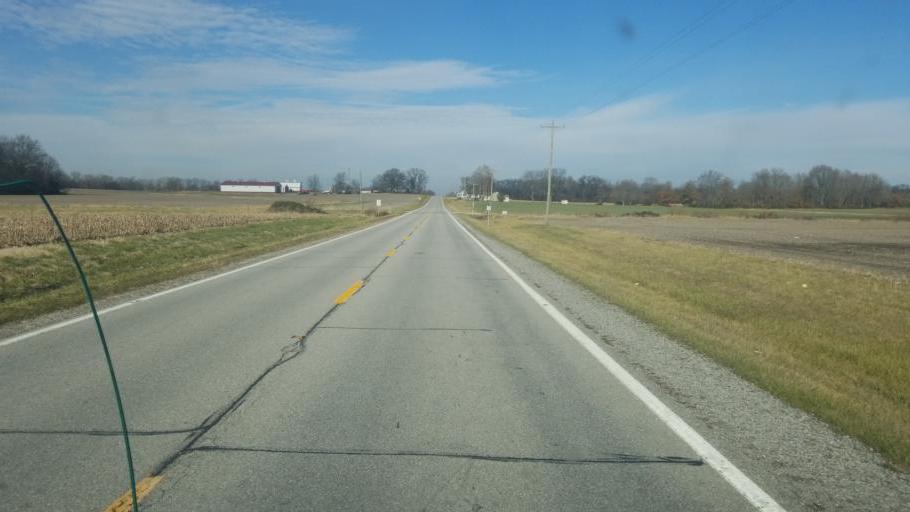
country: US
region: Illinois
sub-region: Saline County
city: Eldorado
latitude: 37.9203
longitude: -88.4576
